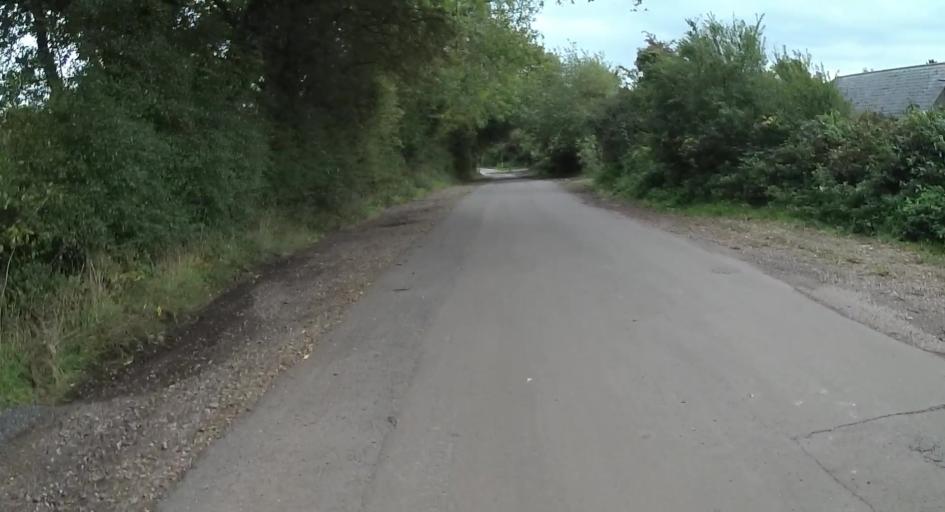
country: GB
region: England
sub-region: Hampshire
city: Four Marks
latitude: 51.0988
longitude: -1.0496
